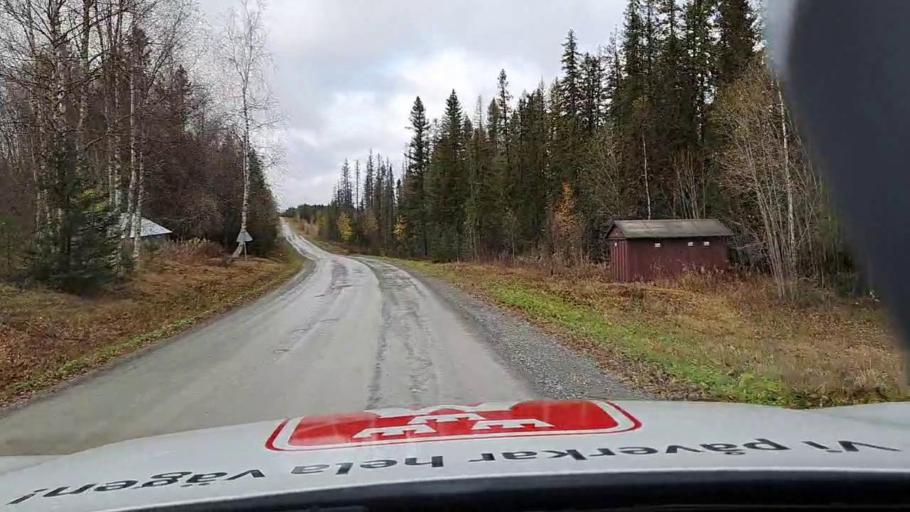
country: SE
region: Jaemtland
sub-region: Bergs Kommun
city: Hoverberg
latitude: 63.0037
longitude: 14.1336
